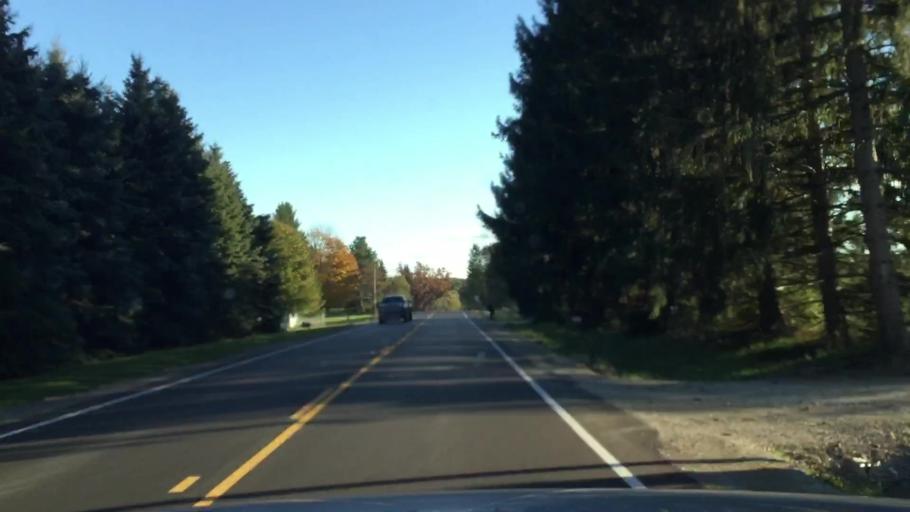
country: US
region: Michigan
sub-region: Lapeer County
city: Almont
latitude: 42.9074
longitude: -83.1430
